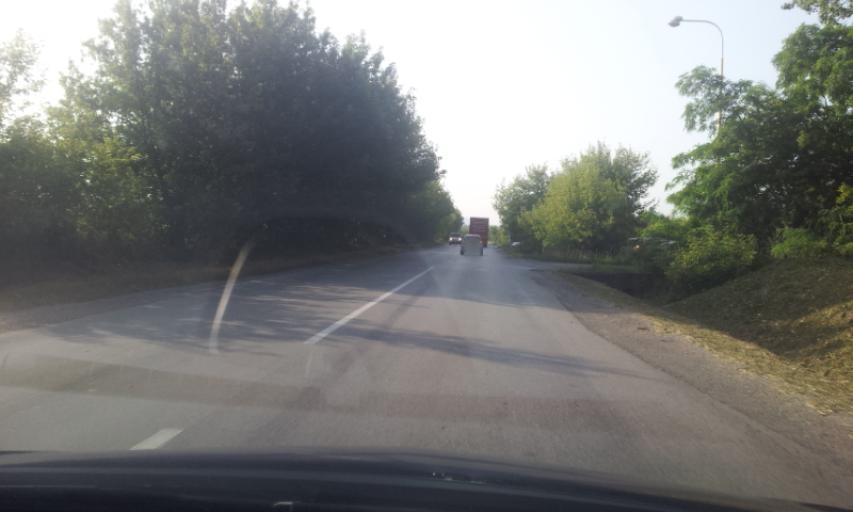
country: SK
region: Kosicky
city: Kosice
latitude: 48.6309
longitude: 21.2168
